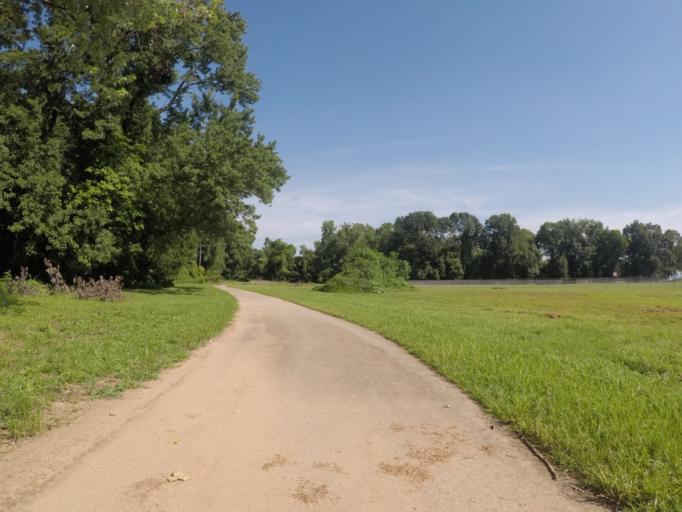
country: US
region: West Virginia
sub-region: Cabell County
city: Huntington
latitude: 38.4034
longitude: -82.4870
